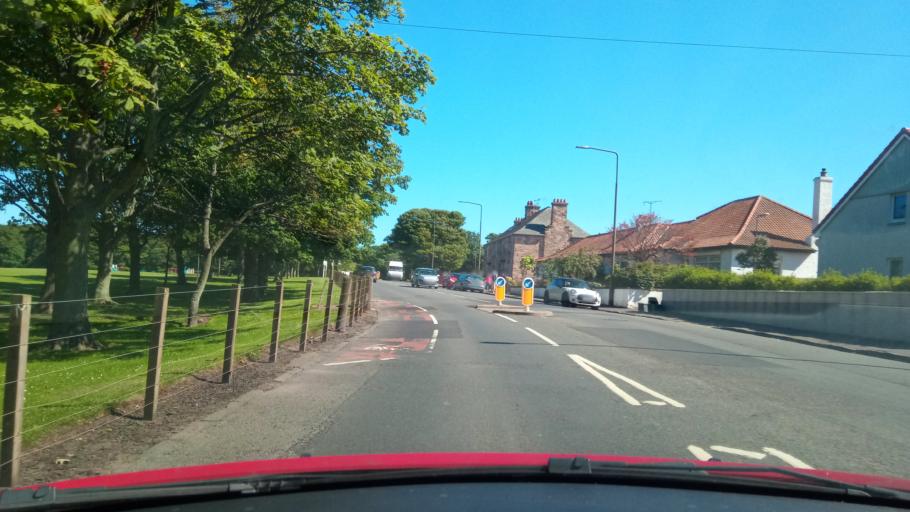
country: GB
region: Scotland
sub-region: East Lothian
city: North Berwick
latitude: 56.0544
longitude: -2.7087
